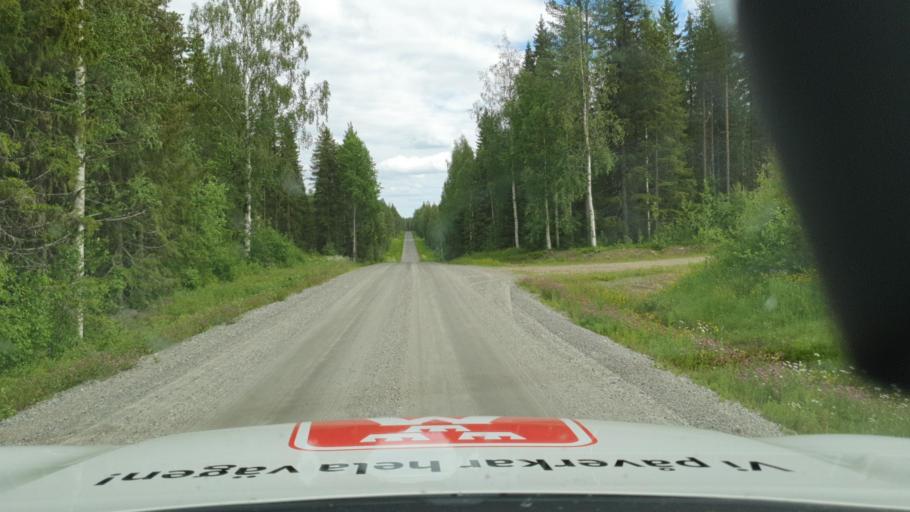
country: SE
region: Vaesterbotten
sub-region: Norsjo Kommun
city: Norsjoe
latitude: 64.8059
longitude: 19.6190
